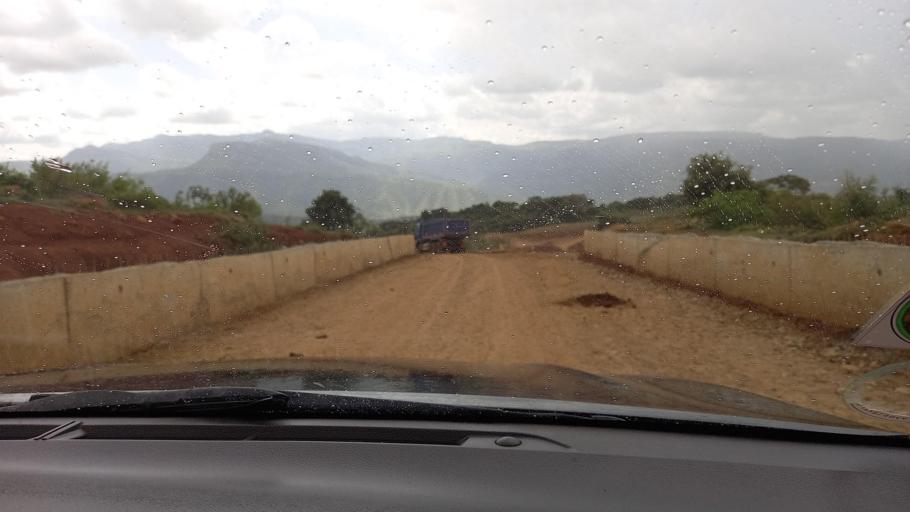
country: ET
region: Southern Nations, Nationalities, and People's Region
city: Mizan Teferi
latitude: 6.1724
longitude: 35.7150
